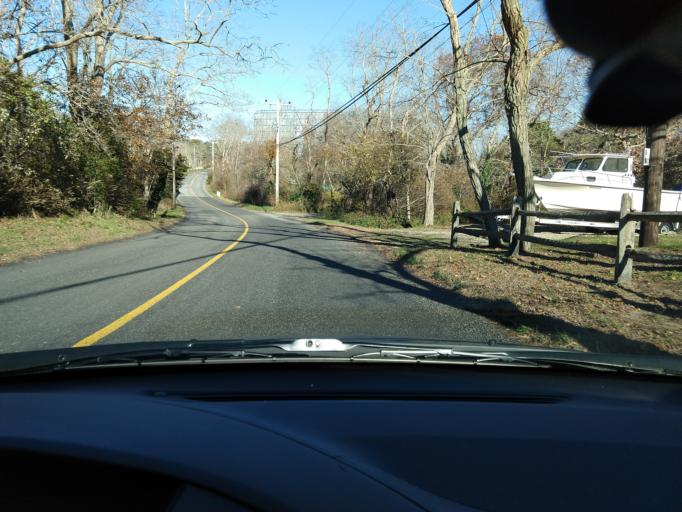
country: US
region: Massachusetts
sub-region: Barnstable County
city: North Eastham
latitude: 41.8756
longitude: -69.9938
